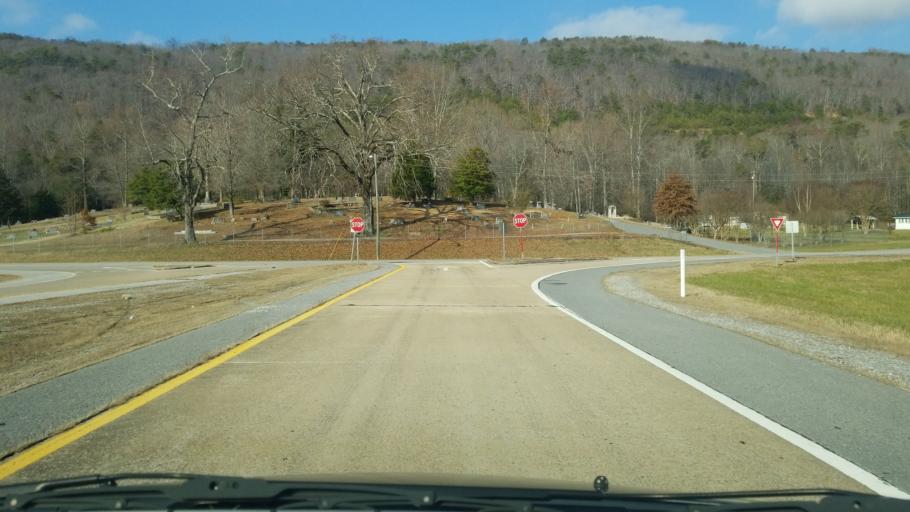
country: US
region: Tennessee
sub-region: Hamilton County
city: Soddy-Daisy
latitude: 35.3053
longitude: -85.1610
